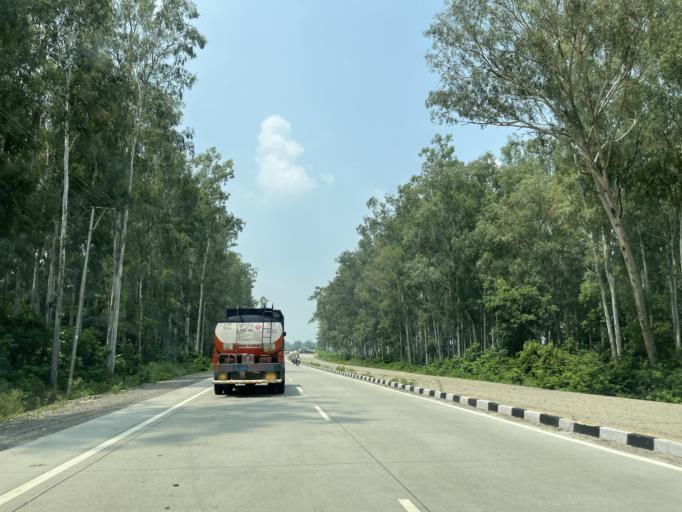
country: IN
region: Uttarakhand
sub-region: Haridwar
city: Haridwar
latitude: 29.8355
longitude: 78.1980
